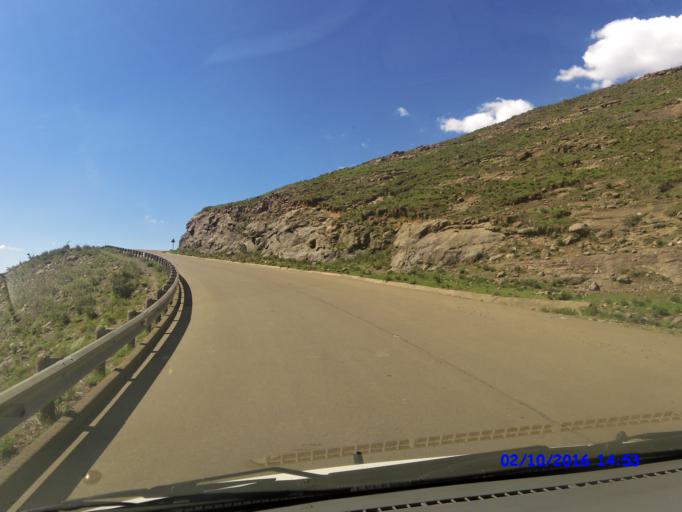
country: LS
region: Maseru
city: Nako
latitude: -29.4792
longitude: 28.0805
